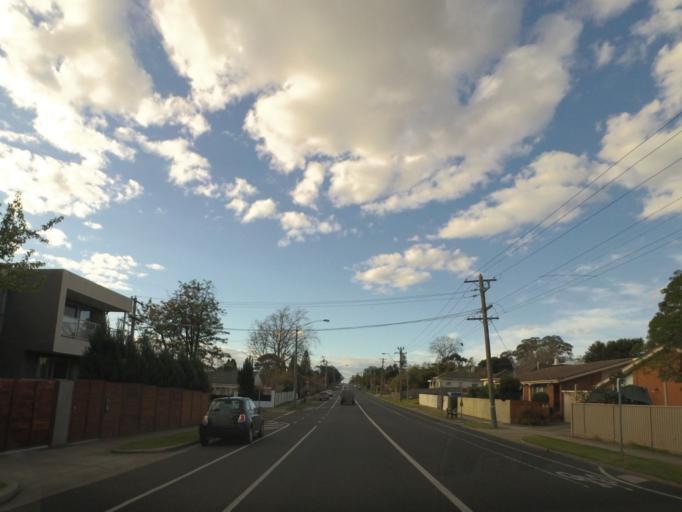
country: AU
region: Victoria
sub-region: Boroondara
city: Canterbury
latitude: -37.8106
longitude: 145.0818
